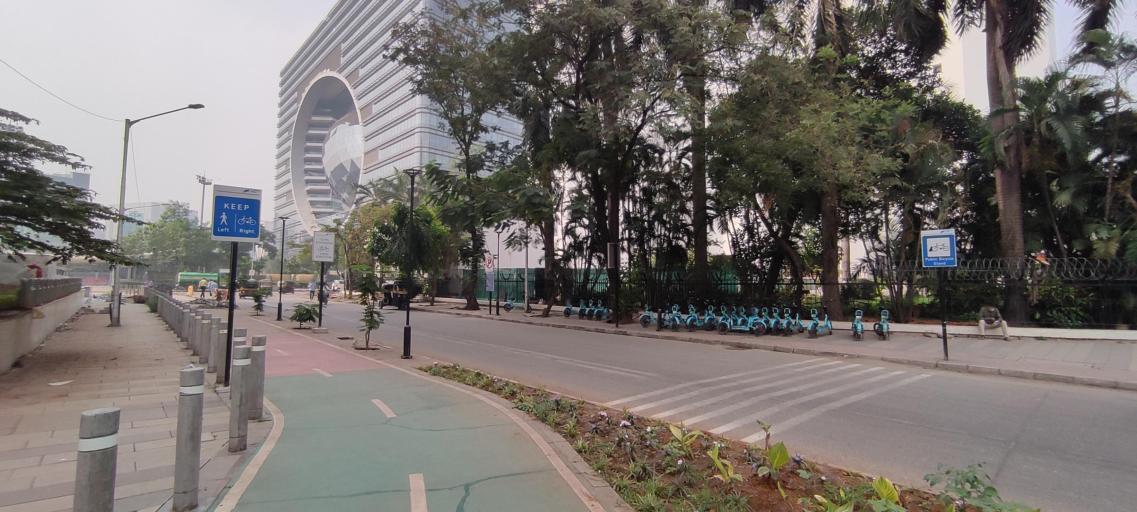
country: IN
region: Maharashtra
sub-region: Mumbai Suburban
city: Mumbai
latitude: 19.0639
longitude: 72.8634
